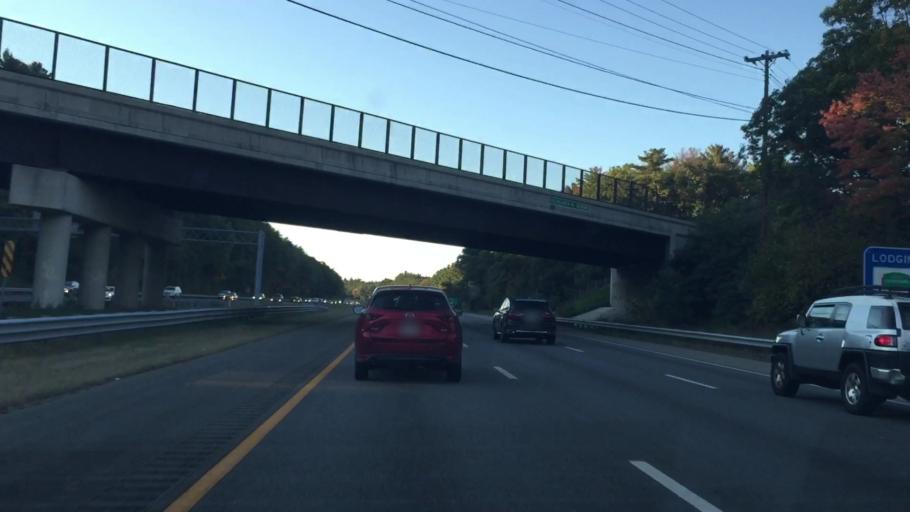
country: US
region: Massachusetts
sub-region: Middlesex County
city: Bedford
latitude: 42.5178
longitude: -71.2588
